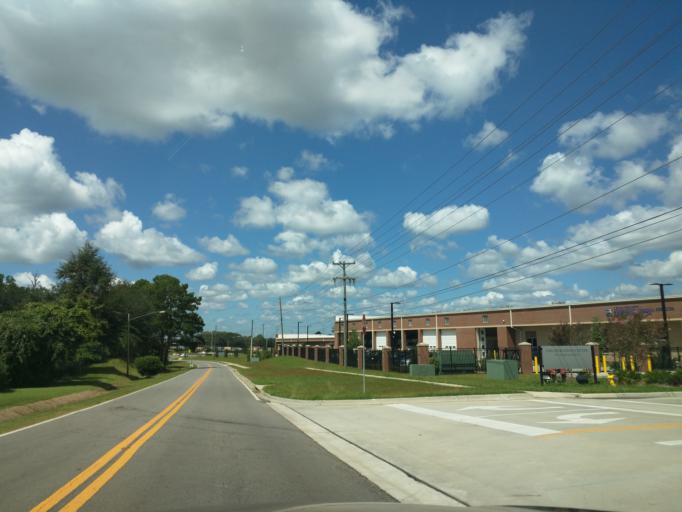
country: US
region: Florida
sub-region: Leon County
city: Tallahassee
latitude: 30.4499
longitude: -84.2213
